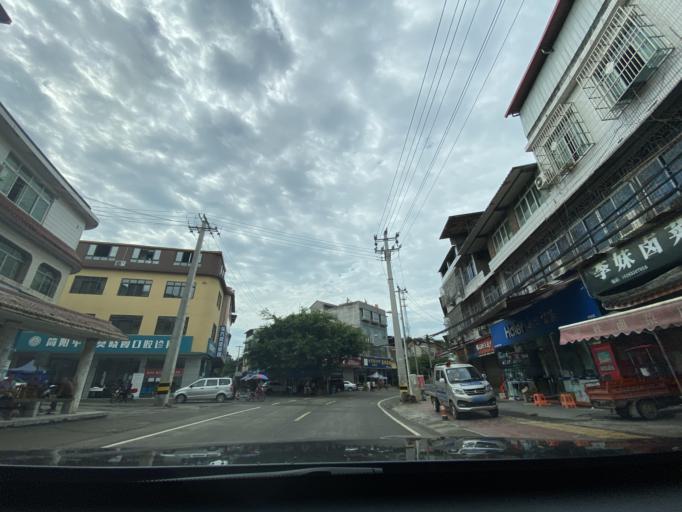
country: CN
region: Sichuan
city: Jiancheng
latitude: 30.4316
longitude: 104.6377
